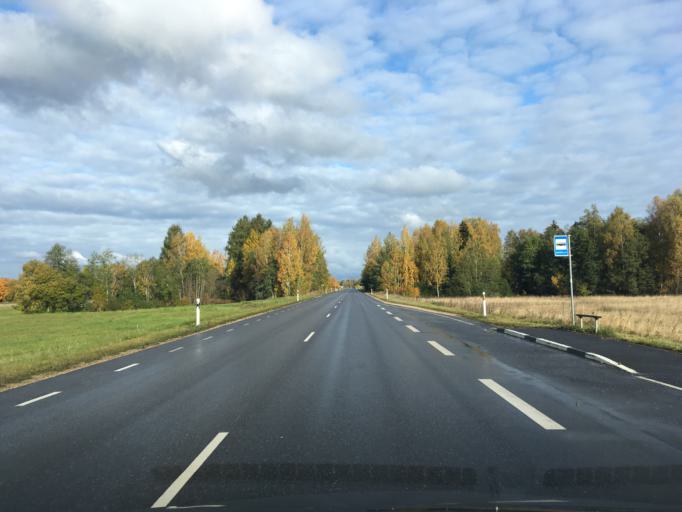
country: EE
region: Harju
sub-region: Raasiku vald
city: Raasiku
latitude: 59.1953
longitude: 25.1853
